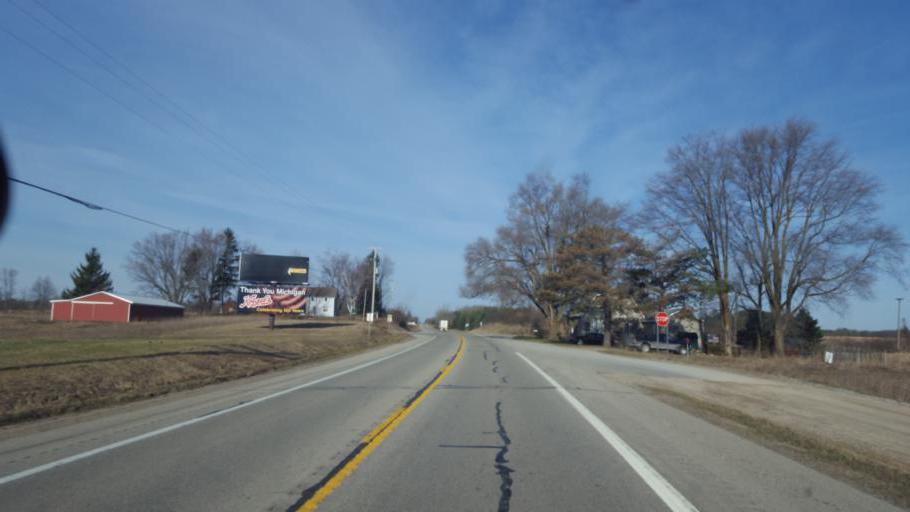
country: US
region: Michigan
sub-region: Montcalm County
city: Lakeview
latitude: 43.4300
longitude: -85.1620
